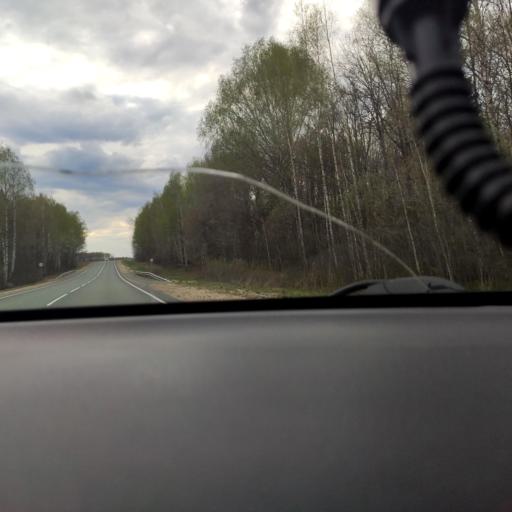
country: RU
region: Mariy-El
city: Krasnogorskiy
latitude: 56.1866
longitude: 48.2498
